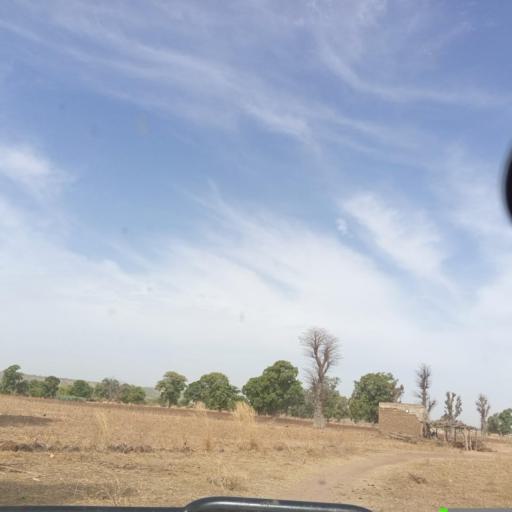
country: ML
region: Koulikoro
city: Koulikoro
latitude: 13.1244
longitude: -7.7064
